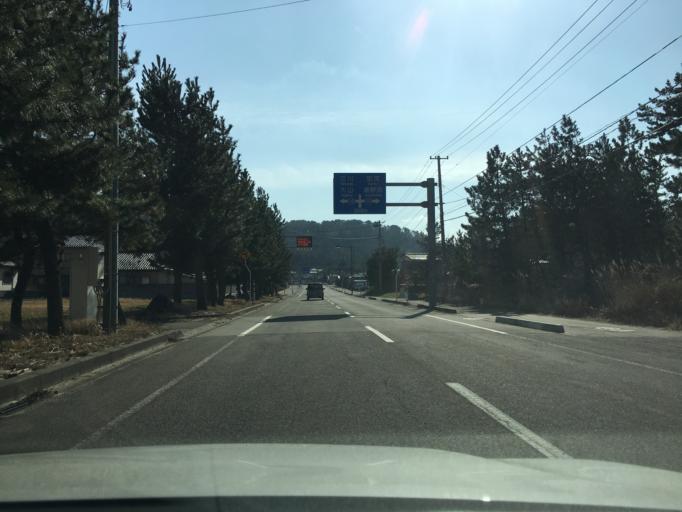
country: JP
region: Yamagata
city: Tsuruoka
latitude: 38.7893
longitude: 139.7667
